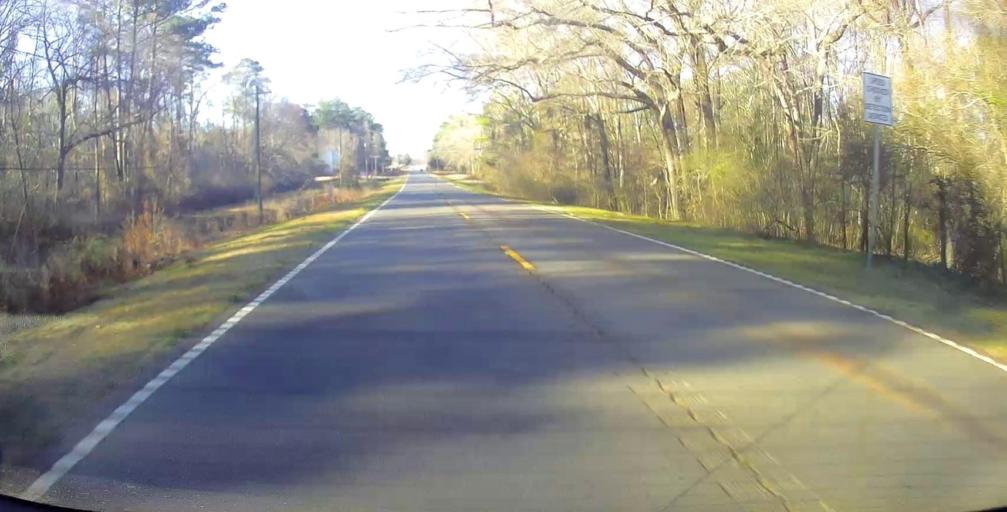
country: US
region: Georgia
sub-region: Sumter County
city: Americus
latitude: 32.0392
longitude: -84.2210
